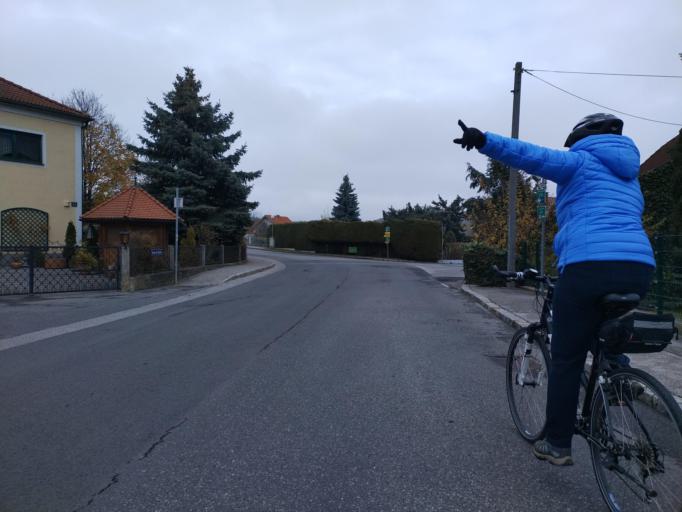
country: AT
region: Lower Austria
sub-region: Politischer Bezirk Neunkirchen
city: Pitten
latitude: 47.7210
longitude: 16.1907
